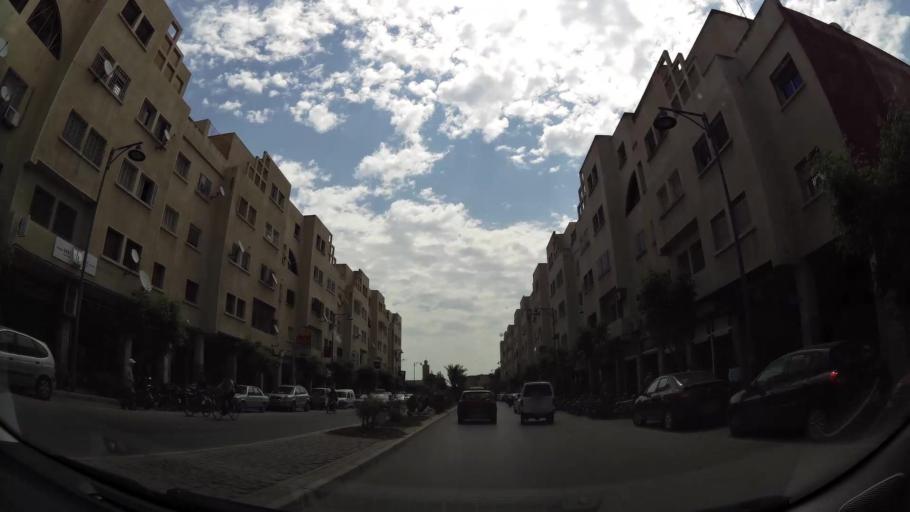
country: MA
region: Oriental
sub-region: Oujda-Angad
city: Oujda
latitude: 34.6795
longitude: -1.9014
